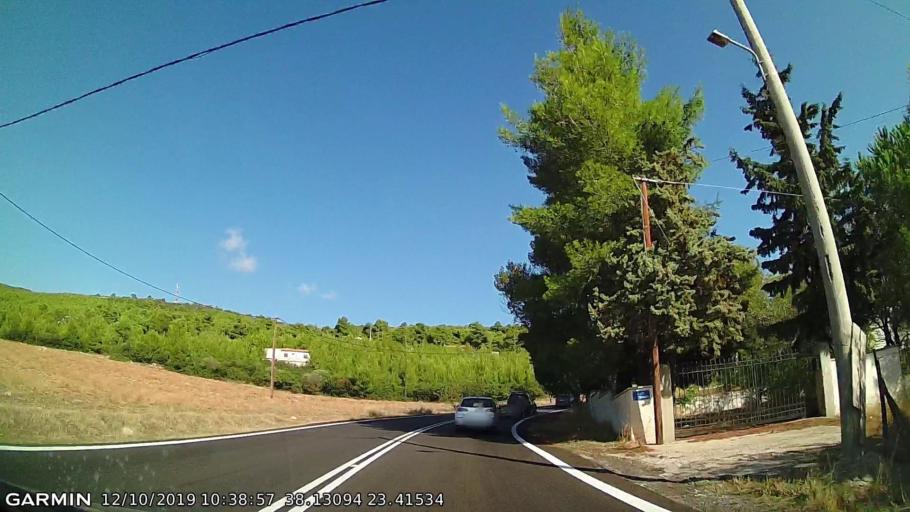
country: GR
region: Attica
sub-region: Nomarchia Dytikis Attikis
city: Vilia
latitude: 38.1311
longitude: 23.4153
